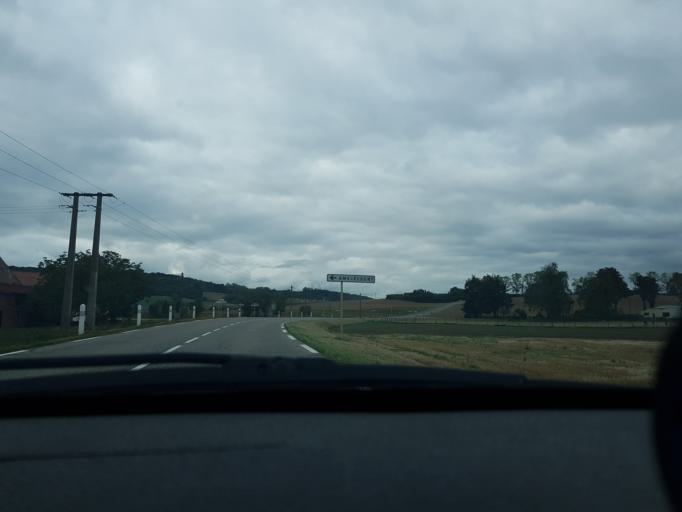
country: FR
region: Lorraine
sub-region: Departement de la Moselle
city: Chateau-Salins
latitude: 48.8384
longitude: 6.5050
